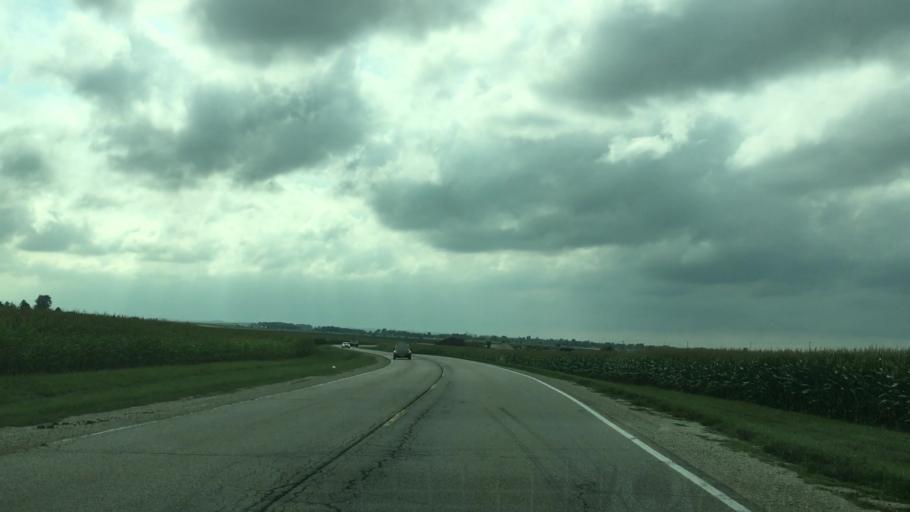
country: US
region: Illinois
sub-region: Ogle County
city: Rochelle
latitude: 41.8978
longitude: -89.0588
